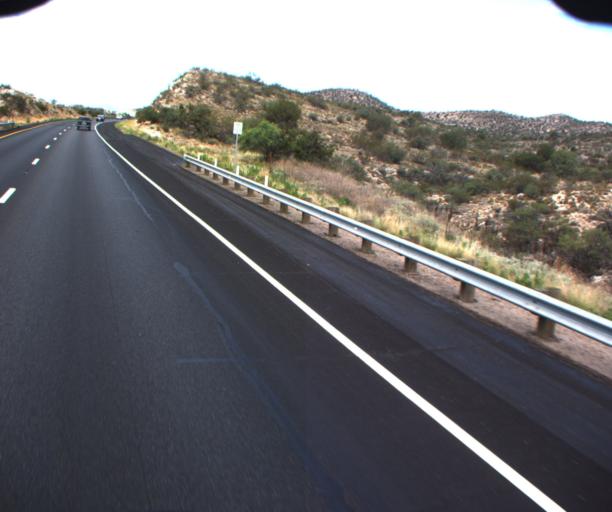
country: US
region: Arizona
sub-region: Yavapai County
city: Lake Montezuma
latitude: 34.6375
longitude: -111.8222
